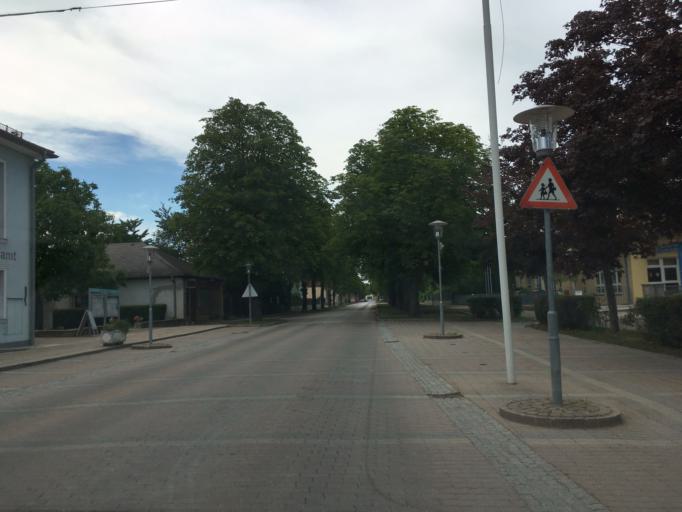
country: AT
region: Lower Austria
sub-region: Politischer Bezirk Baden
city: Teesdorf
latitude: 47.9486
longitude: 16.2834
